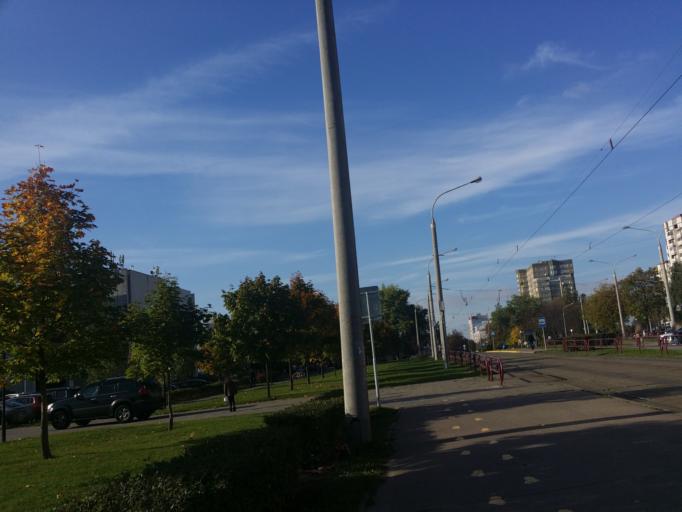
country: BY
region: Minsk
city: Minsk
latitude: 53.9245
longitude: 27.5460
